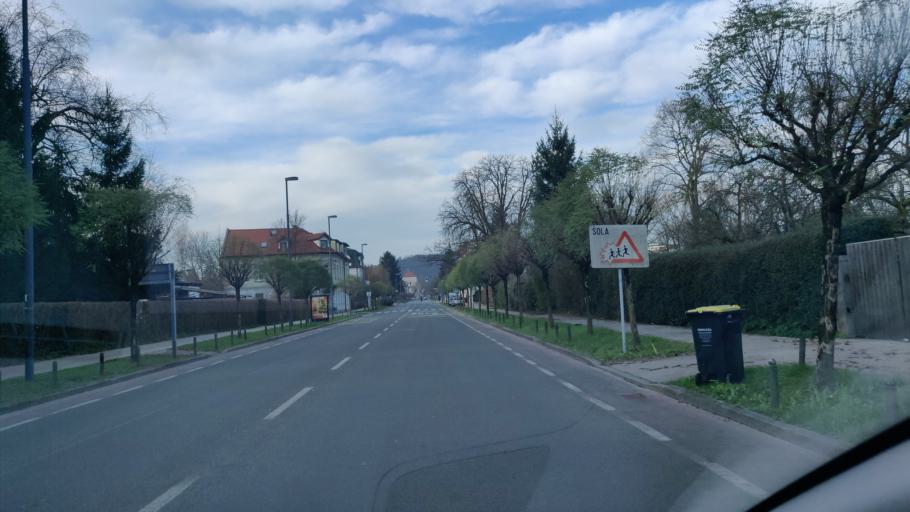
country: SI
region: Ljubljana
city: Ljubljana
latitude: 46.0422
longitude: 14.4987
